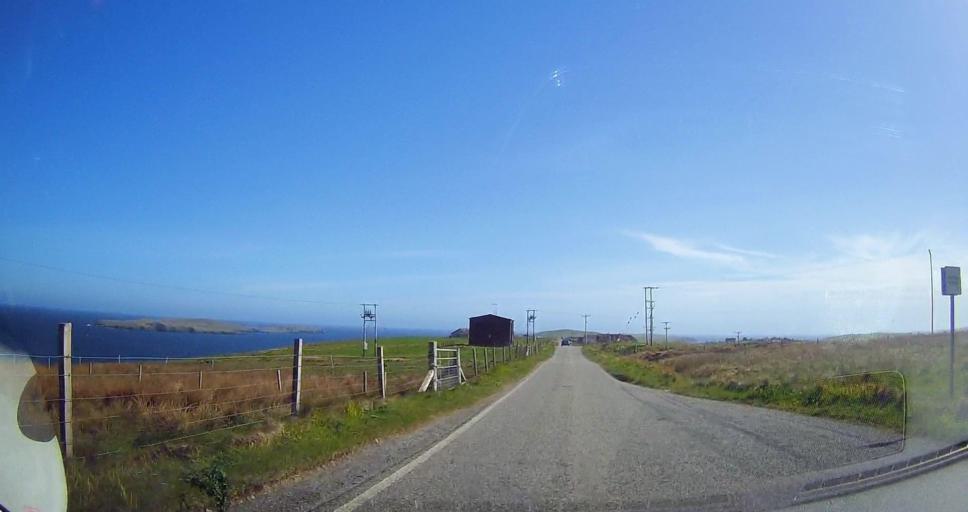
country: GB
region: Scotland
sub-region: Shetland Islands
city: Sandwick
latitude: 60.0173
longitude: -1.2301
